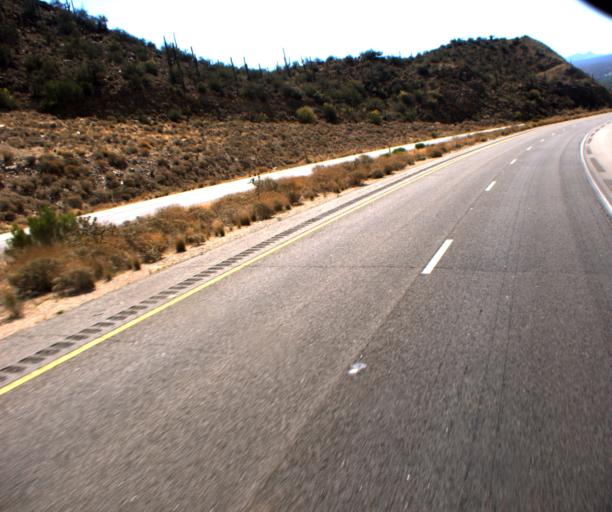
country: US
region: Arizona
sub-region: Yavapai County
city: Bagdad
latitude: 34.4097
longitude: -113.2276
